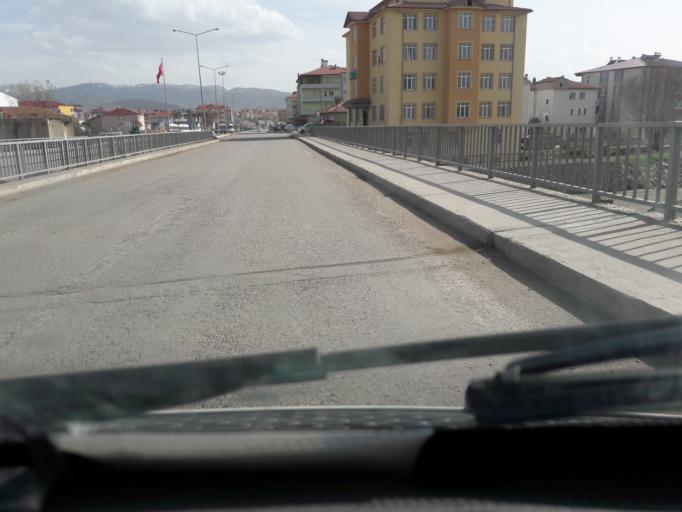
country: TR
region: Gumushane
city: Kelkit
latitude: 40.1371
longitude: 39.4333
